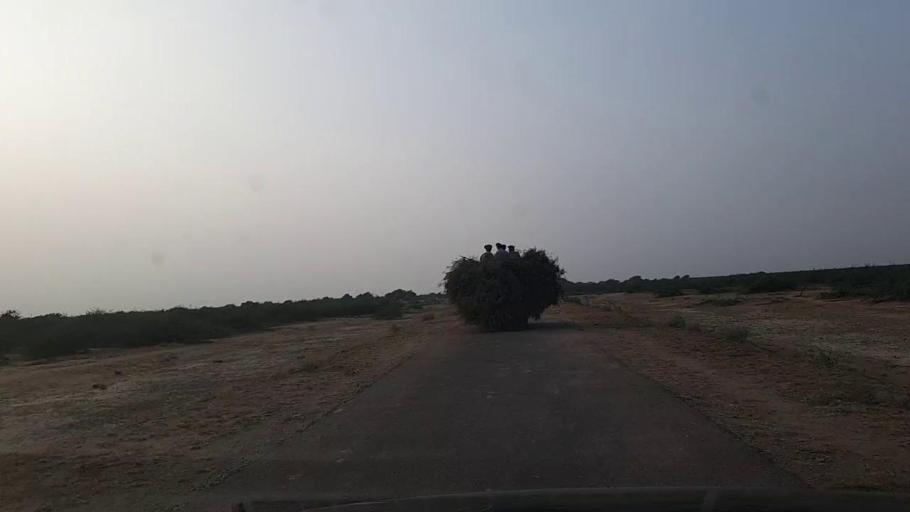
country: PK
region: Sindh
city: Gharo
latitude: 24.7833
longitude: 67.7268
